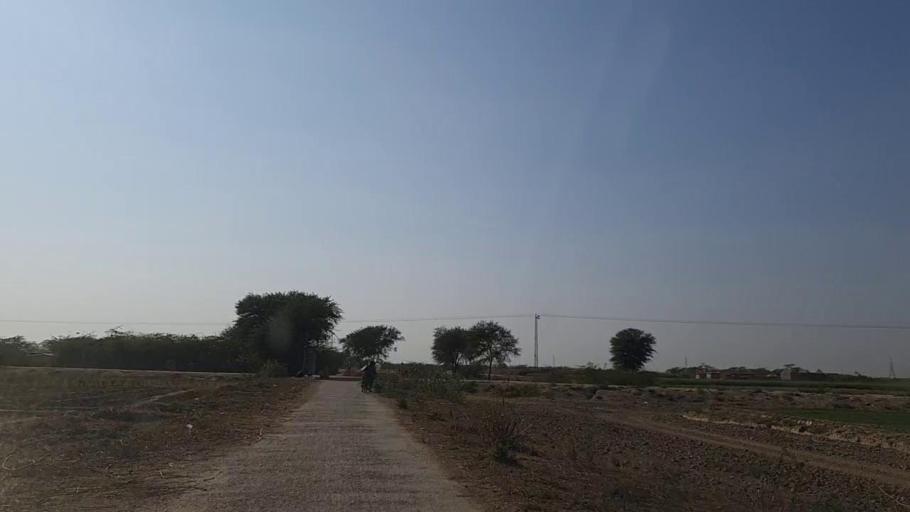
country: PK
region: Sindh
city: Naukot
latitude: 24.9571
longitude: 69.4797
